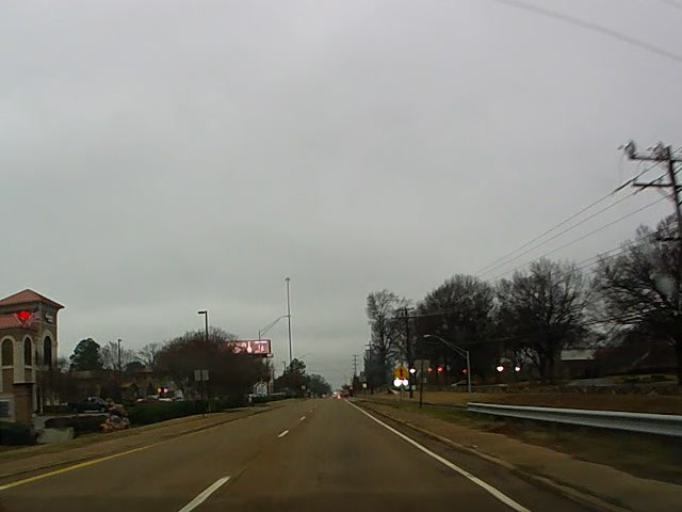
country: US
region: Tennessee
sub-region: Shelby County
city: Germantown
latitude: 35.1046
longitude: -89.8721
